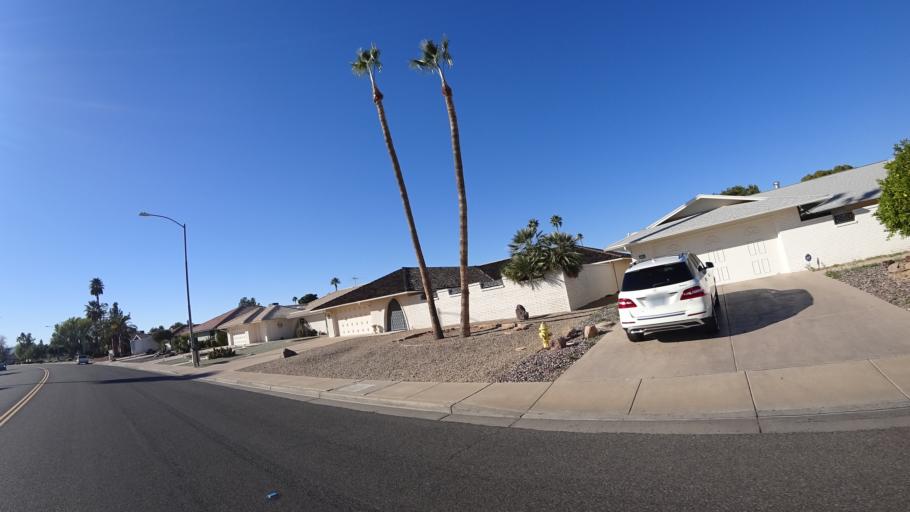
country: US
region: Arizona
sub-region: Maricopa County
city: Sun City West
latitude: 33.6723
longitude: -112.3493
